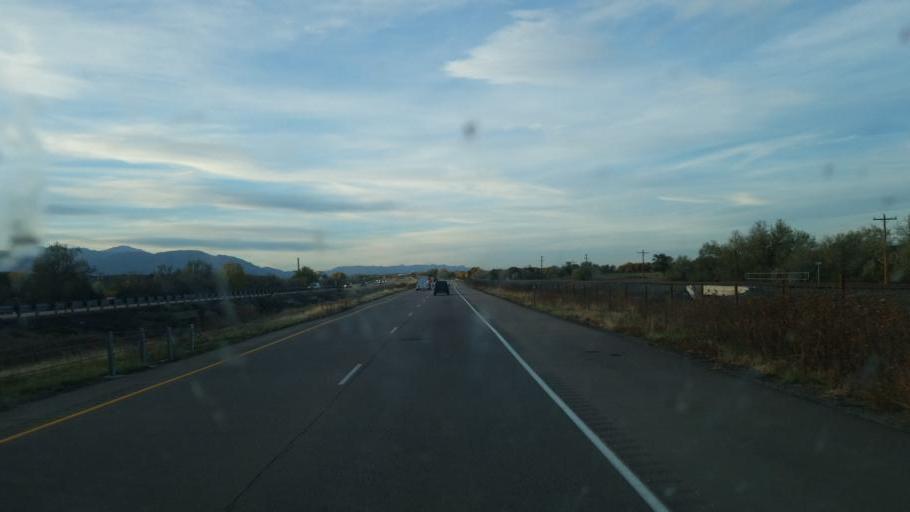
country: US
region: Colorado
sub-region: El Paso County
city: Fountain
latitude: 38.6047
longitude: -104.6789
